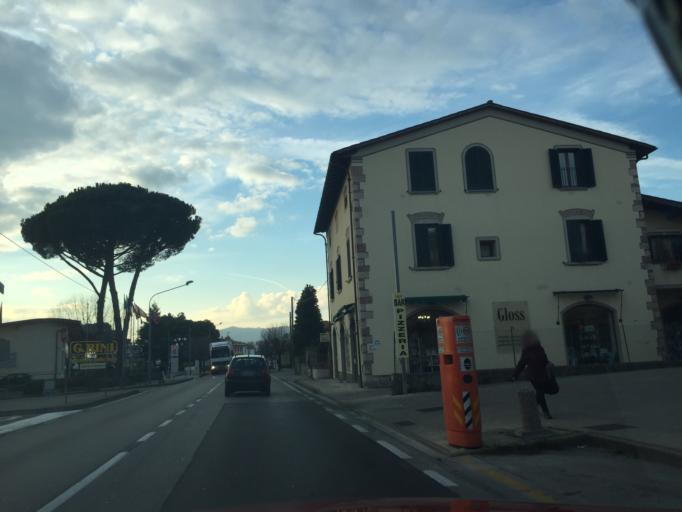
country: IT
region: Tuscany
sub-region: Provincia di Pistoia
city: Pieve a Nievole
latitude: 43.8741
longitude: 10.8029
